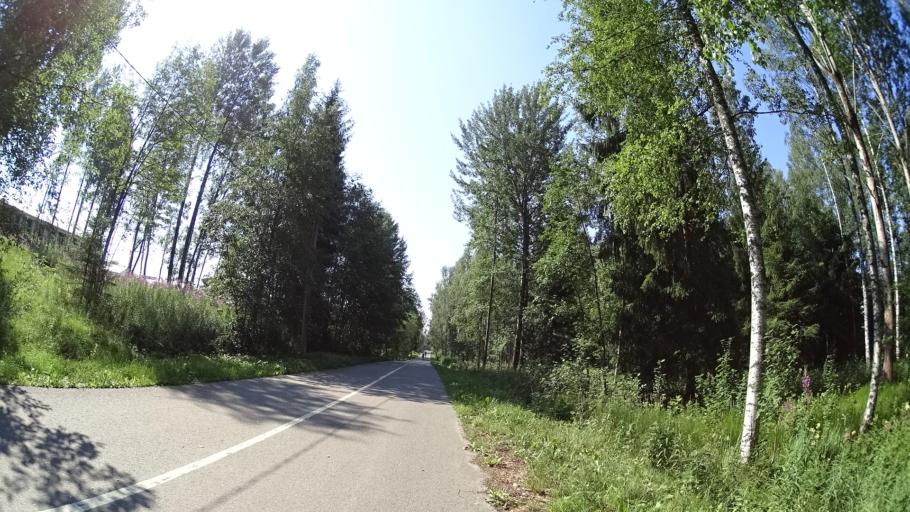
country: FI
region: Uusimaa
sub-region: Helsinki
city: Kerava
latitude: 60.3847
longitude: 25.0940
